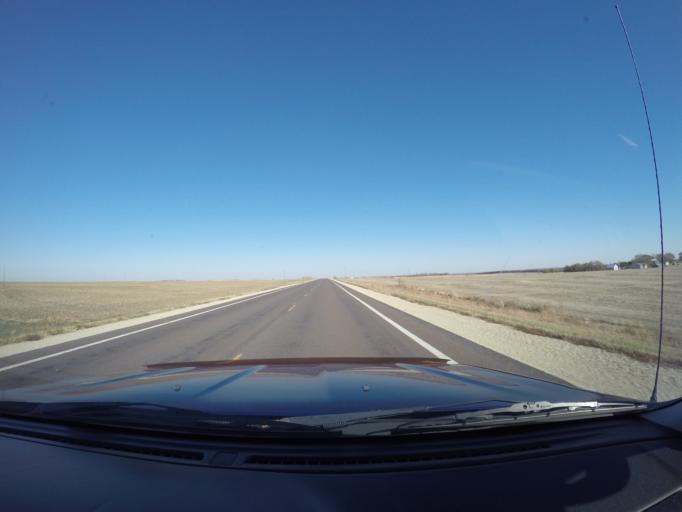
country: US
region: Kansas
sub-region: Marshall County
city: Blue Rapids
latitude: 39.6366
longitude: -96.7504
